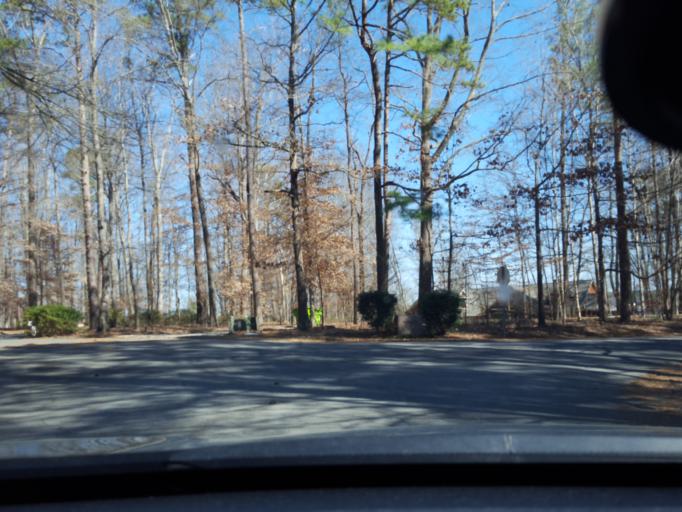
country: US
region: North Carolina
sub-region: Halifax County
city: South Rosemary
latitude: 36.5090
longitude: -77.8915
